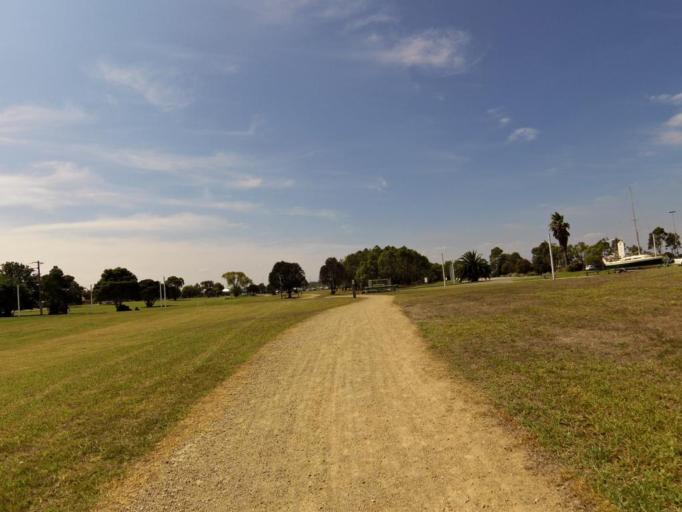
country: AU
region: Victoria
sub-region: Mornington Peninsula
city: Hastings
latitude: -38.3126
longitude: 145.1953
